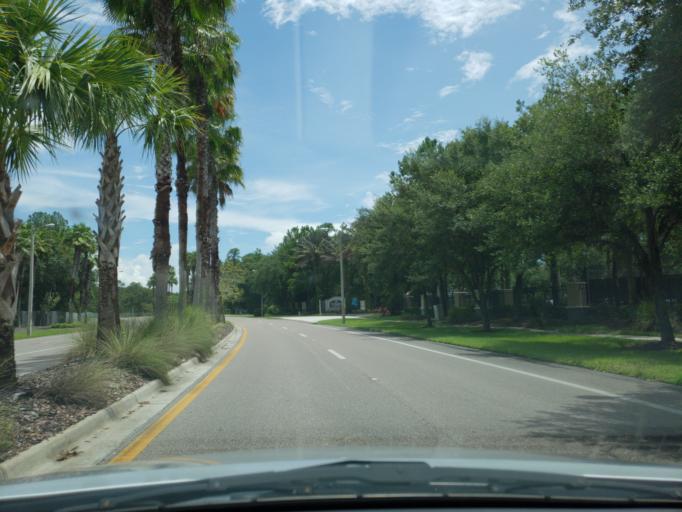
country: US
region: Florida
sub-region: Hillsborough County
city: Pebble Creek
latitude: 28.1266
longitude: -82.3833
